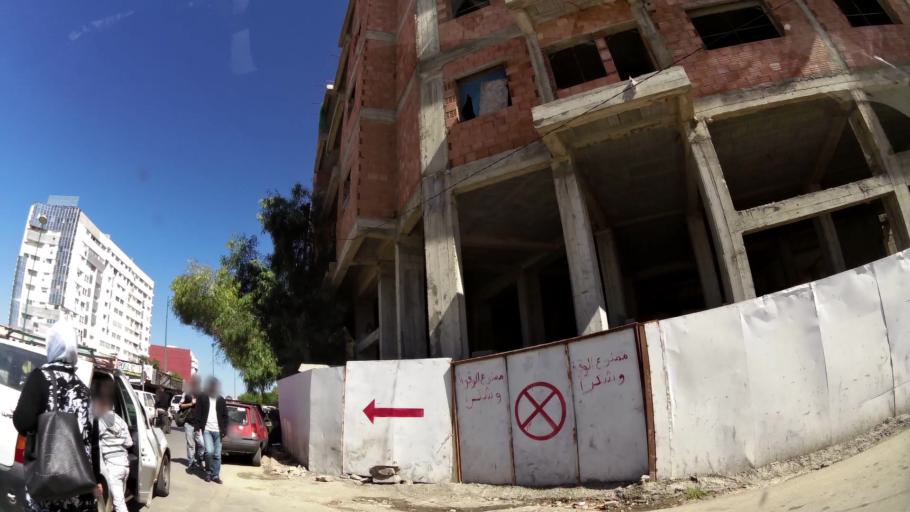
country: MA
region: Meknes-Tafilalet
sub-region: Meknes
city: Meknes
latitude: 33.8965
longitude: -5.5417
